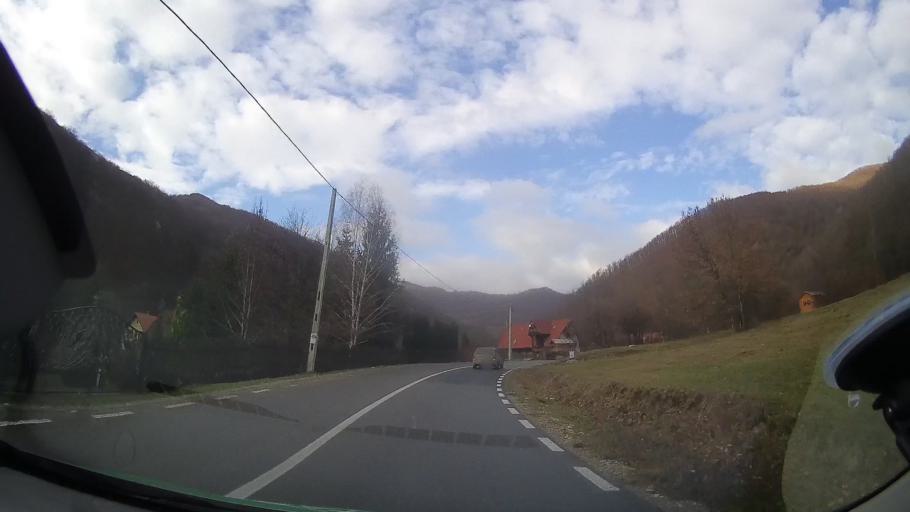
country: RO
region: Cluj
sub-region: Comuna Baisoara
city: Baisoara
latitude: 46.6105
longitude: 23.4135
